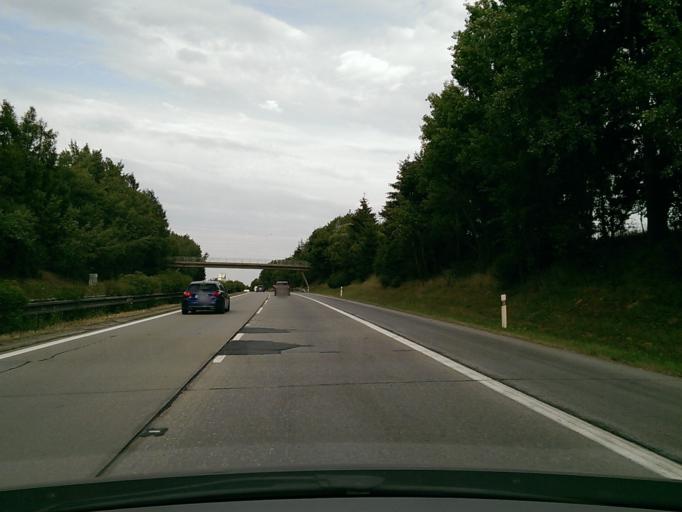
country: CZ
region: Vysocina
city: Kamenice
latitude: 49.4074
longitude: 15.7791
